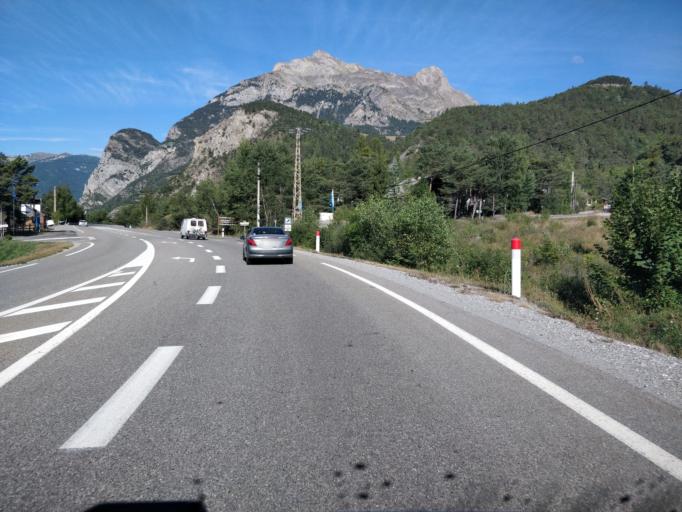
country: FR
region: Provence-Alpes-Cote d'Azur
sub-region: Departement des Alpes-de-Haute-Provence
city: Barcelonnette
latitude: 44.3995
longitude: 6.5326
